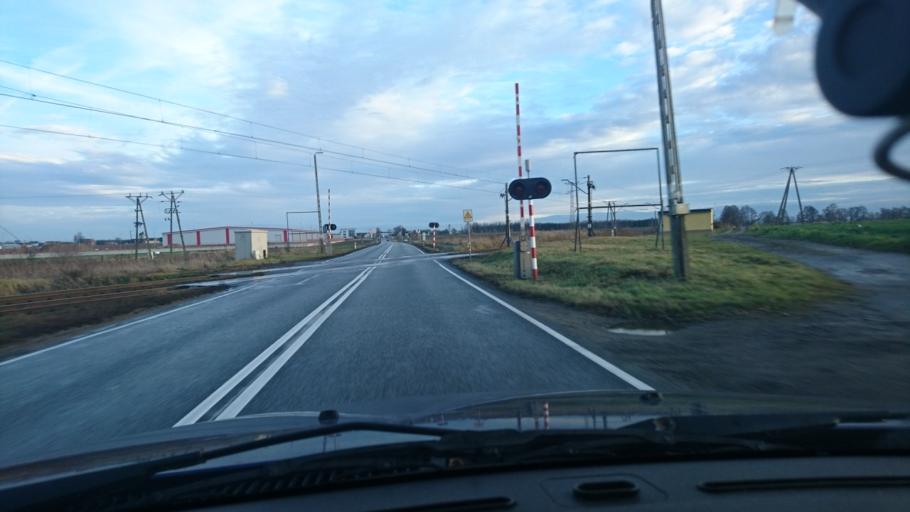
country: PL
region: Greater Poland Voivodeship
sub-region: Powiat kepinski
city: Slupia pod Kepnem
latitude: 51.2328
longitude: 18.0642
